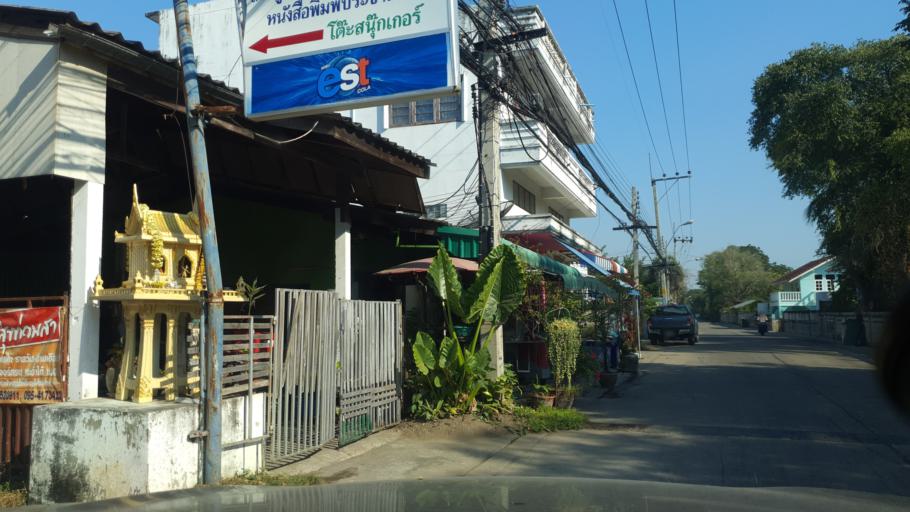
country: TH
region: Phetchaburi
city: Cha-am
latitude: 12.7853
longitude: 99.9784
